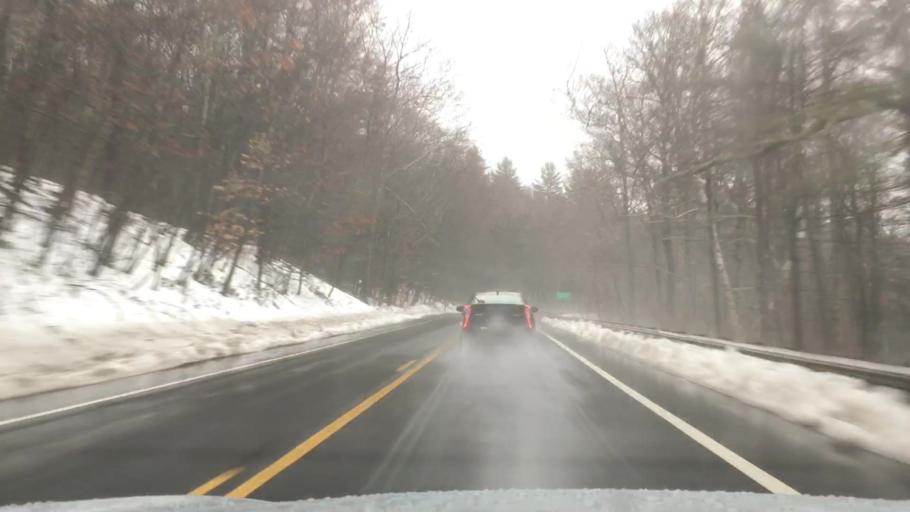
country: US
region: Massachusetts
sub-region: Franklin County
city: Shutesbury
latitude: 42.4467
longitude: -72.3882
